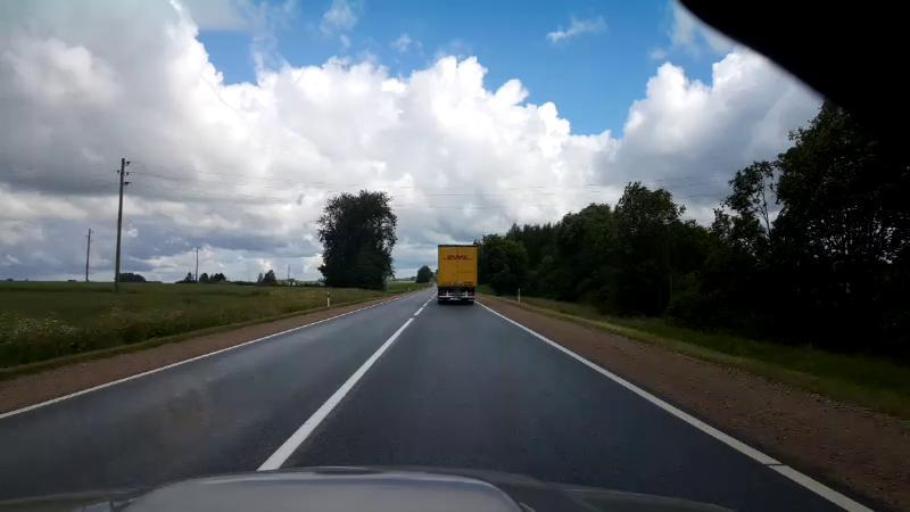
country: LV
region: Bauskas Rajons
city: Bauska
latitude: 56.4987
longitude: 24.1749
